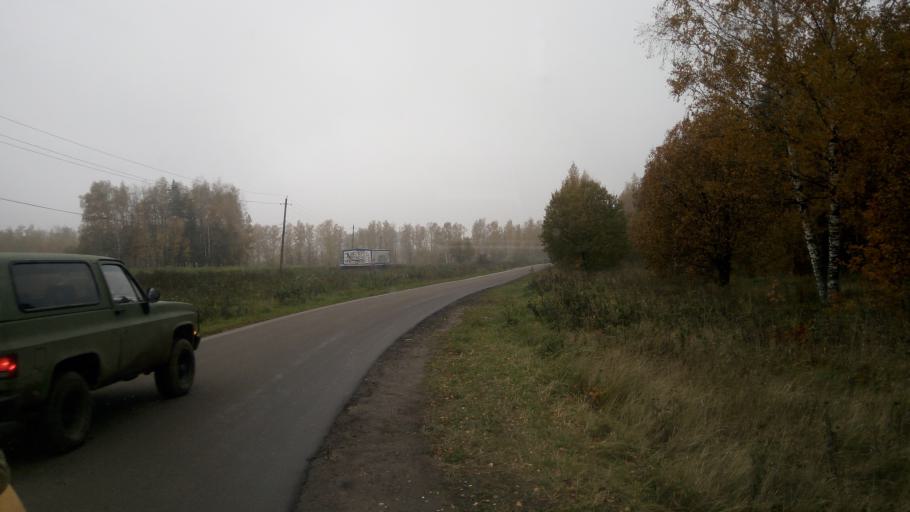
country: RU
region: Moskovskaya
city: Firsanovka
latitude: 55.9269
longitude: 37.2315
